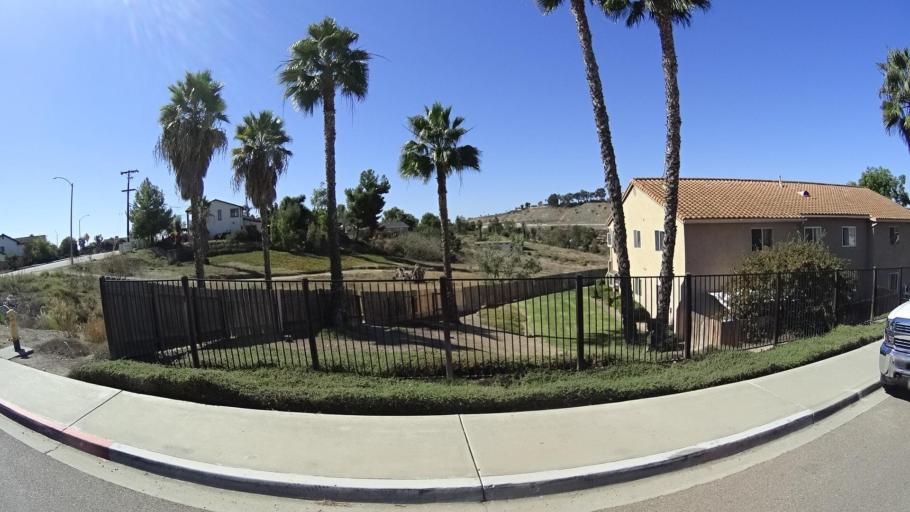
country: US
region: California
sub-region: San Diego County
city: La Presa
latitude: 32.6997
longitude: -117.0053
